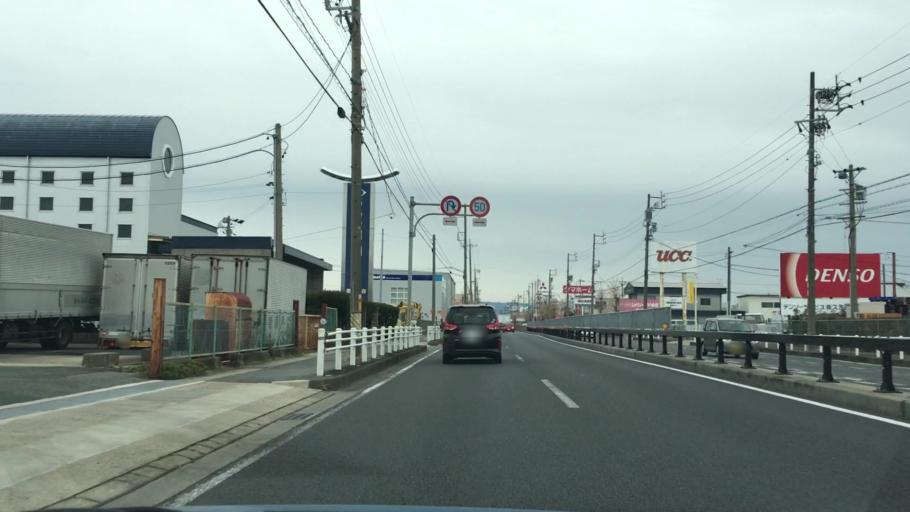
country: JP
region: Aichi
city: Toyohashi
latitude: 34.7818
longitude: 137.3818
